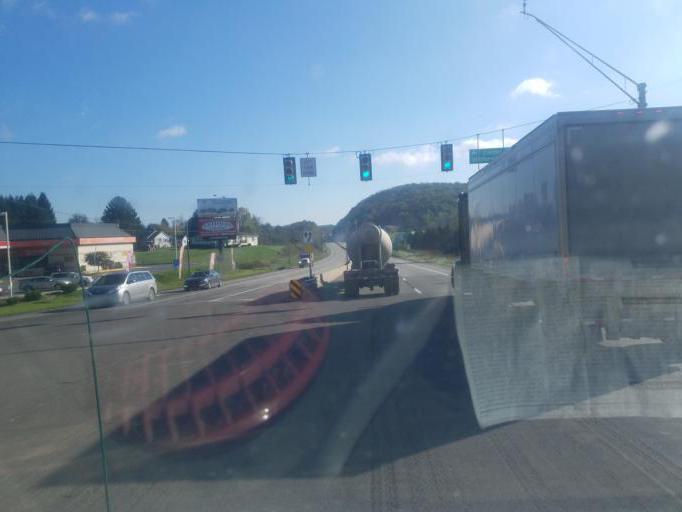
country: US
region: Pennsylvania
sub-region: Cambria County
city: Ebensburg
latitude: 40.4774
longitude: -78.7241
